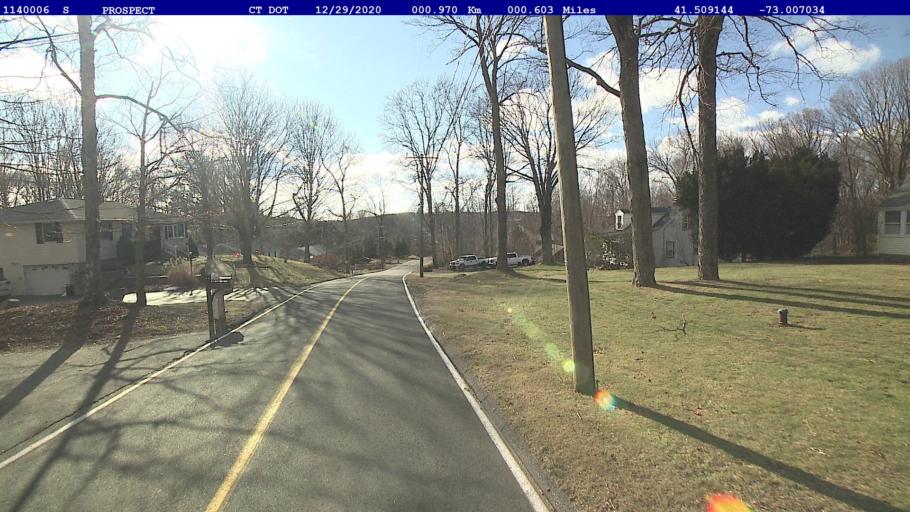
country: US
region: Connecticut
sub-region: New Haven County
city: Prospect
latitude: 41.5091
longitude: -73.0070
